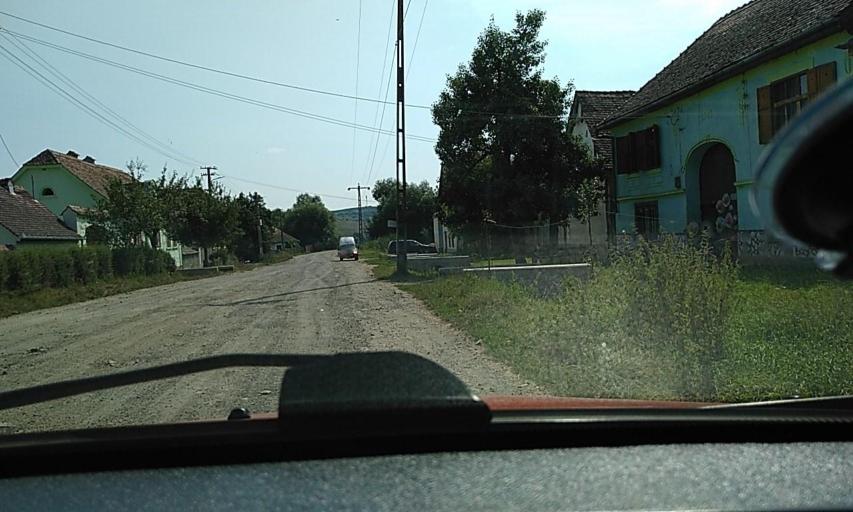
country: RO
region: Brasov
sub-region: Oras Rupea
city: Fiser
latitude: 46.0566
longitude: 25.0995
